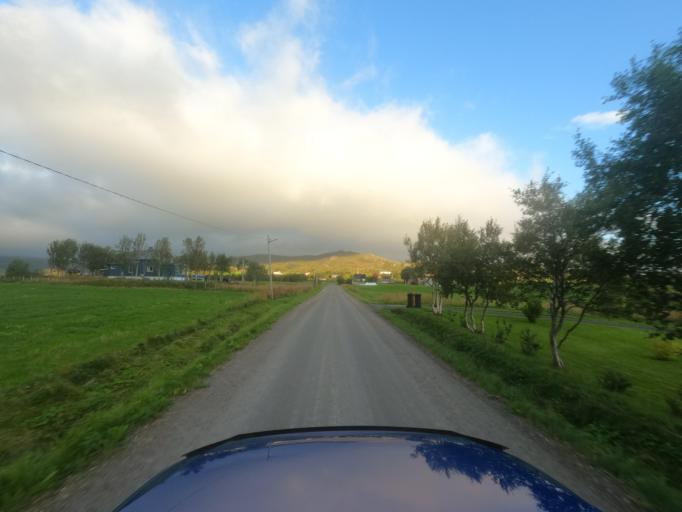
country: NO
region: Nordland
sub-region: Vestvagoy
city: Leknes
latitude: 68.2030
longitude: 13.6679
